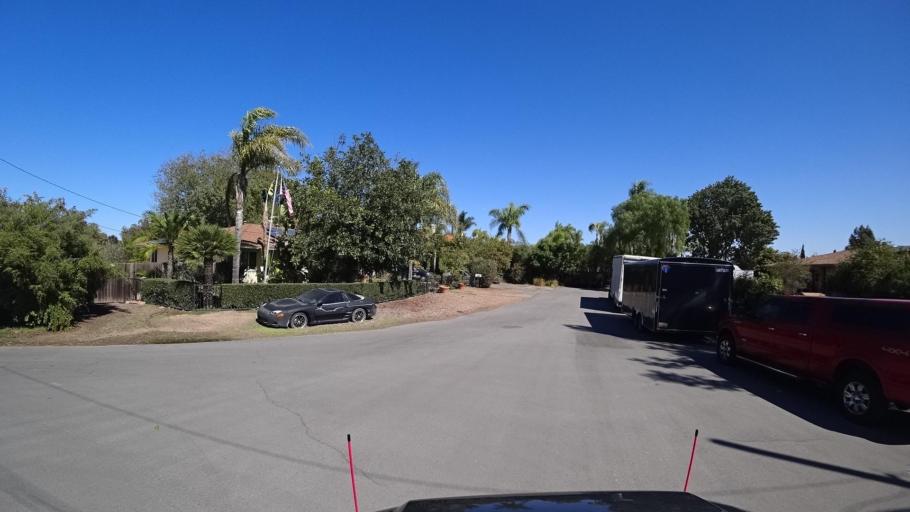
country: US
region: California
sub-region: San Diego County
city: Bonita
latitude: 32.6673
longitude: -117.0442
